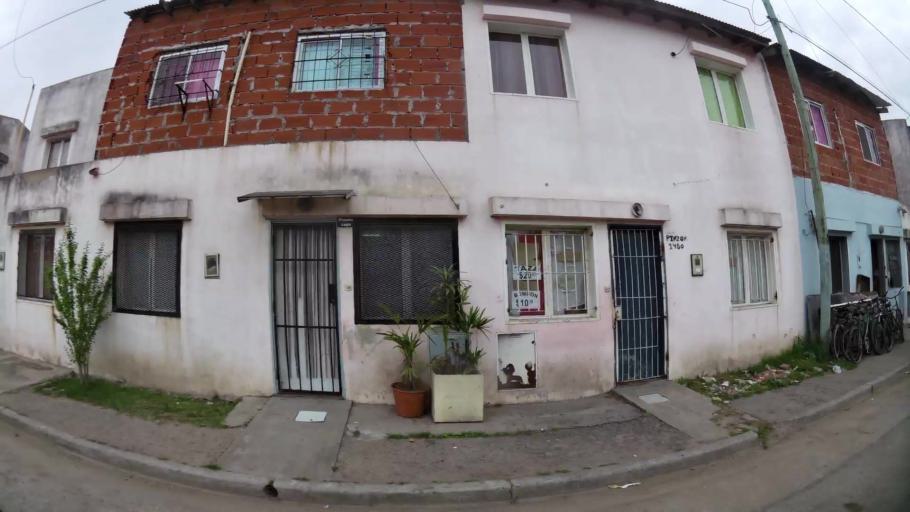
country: AR
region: Buenos Aires
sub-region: Partido de Avellaneda
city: Avellaneda
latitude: -34.6517
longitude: -58.3548
